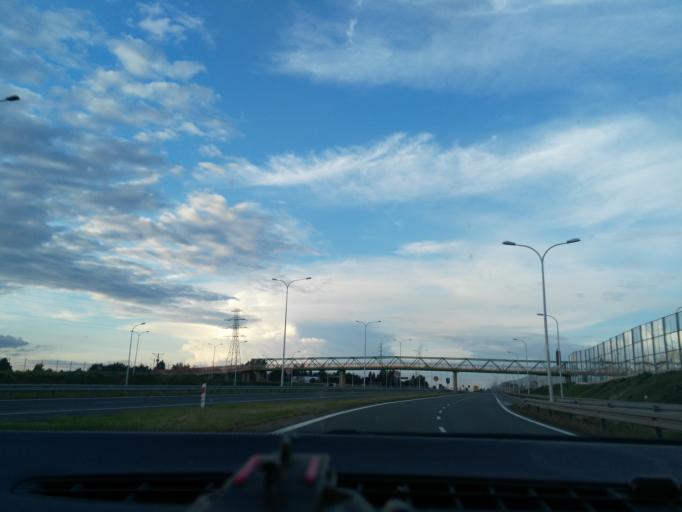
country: PL
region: Lublin Voivodeship
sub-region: Powiat lubelski
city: Jakubowice Murowane
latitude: 51.3037
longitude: 22.5898
